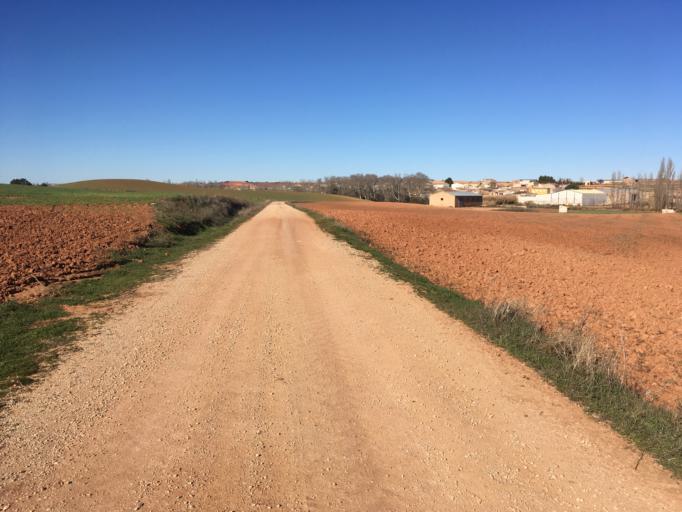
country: ES
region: Castille-La Mancha
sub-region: Provincia de Cuenca
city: Atalaya del Canavate
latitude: 39.5434
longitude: -2.2452
